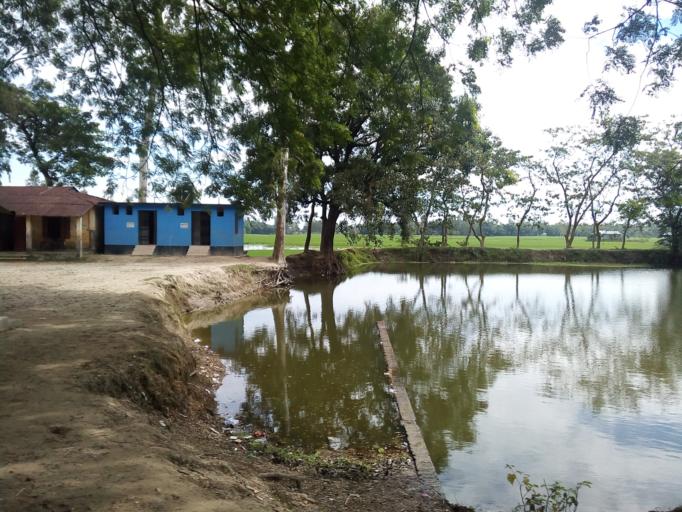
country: BD
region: Rangpur Division
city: Nageswari
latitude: 25.8950
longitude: 89.7103
